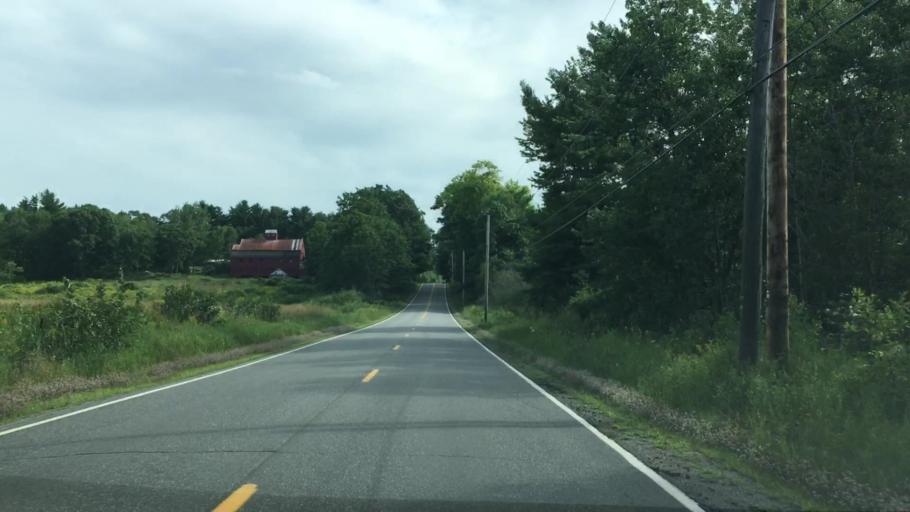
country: US
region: Maine
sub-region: Waldo County
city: Belfast
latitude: 44.3943
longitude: -69.0327
